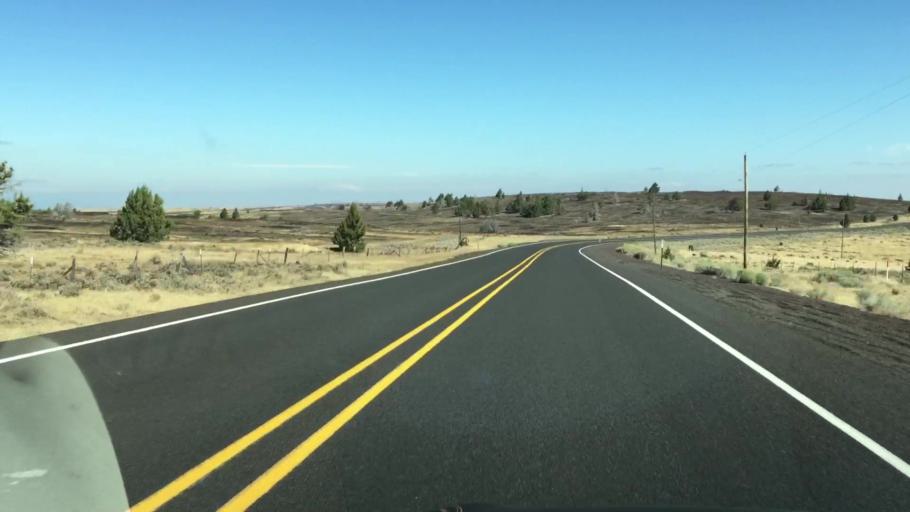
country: US
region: Oregon
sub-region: Jefferson County
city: Warm Springs
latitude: 45.0025
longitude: -120.9957
